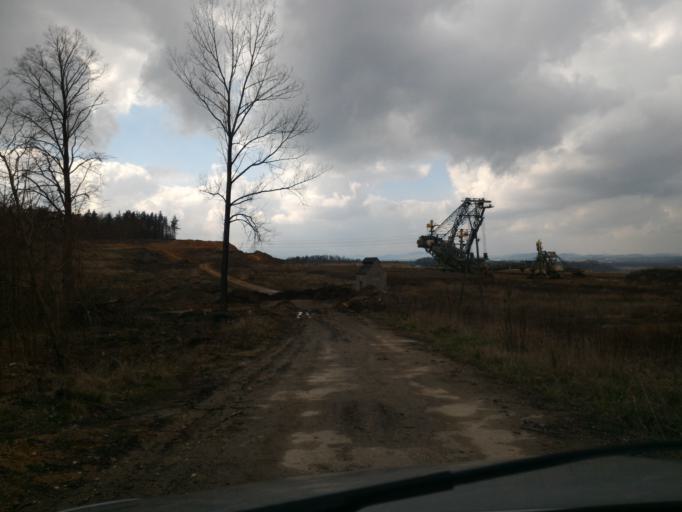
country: PL
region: Lower Silesian Voivodeship
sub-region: Powiat zgorzelecki
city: Bogatynia
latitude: 50.8833
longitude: 14.9007
